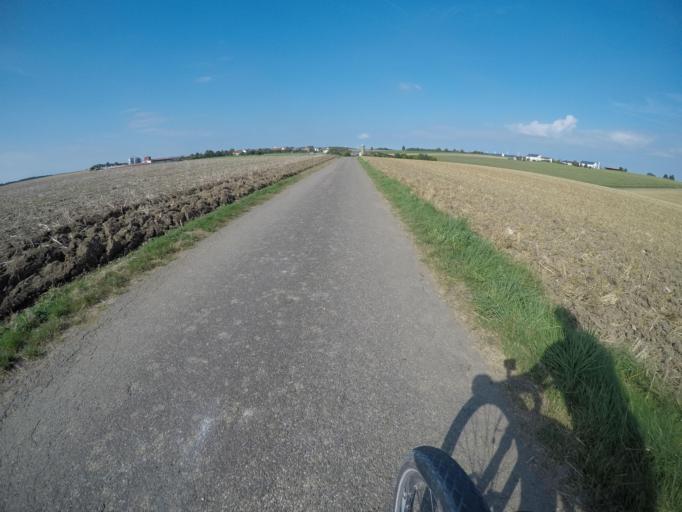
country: DE
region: Baden-Wuerttemberg
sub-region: Regierungsbezirk Stuttgart
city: Bohmenkirch
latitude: 48.6367
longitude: 9.9236
